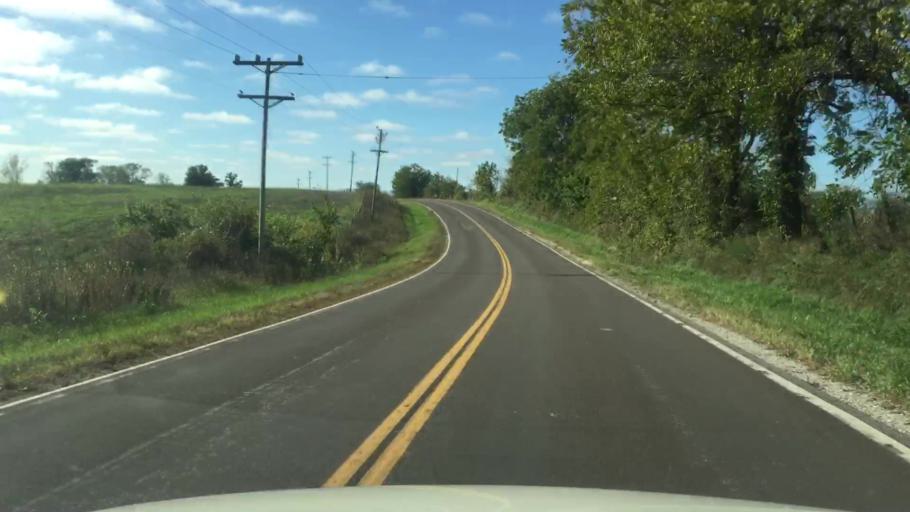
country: US
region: Missouri
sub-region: Howard County
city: New Franklin
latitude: 39.0860
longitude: -92.7453
